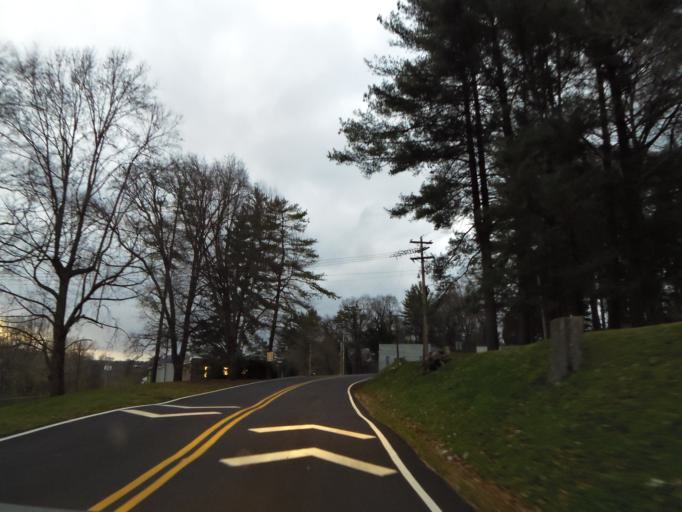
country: US
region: Tennessee
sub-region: Blount County
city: Eagleton Village
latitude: 35.8336
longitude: -83.9442
